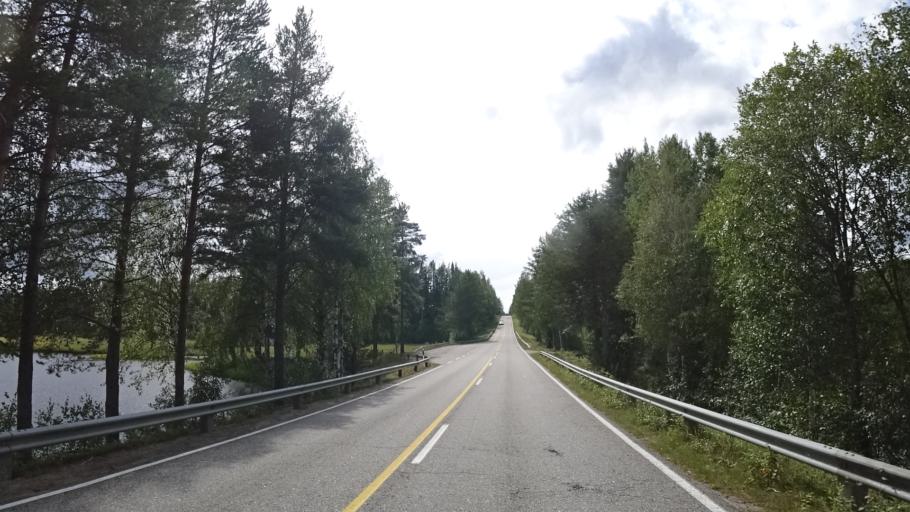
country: FI
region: North Karelia
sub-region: Joensuu
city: Ilomantsi
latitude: 62.7576
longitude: 31.0093
